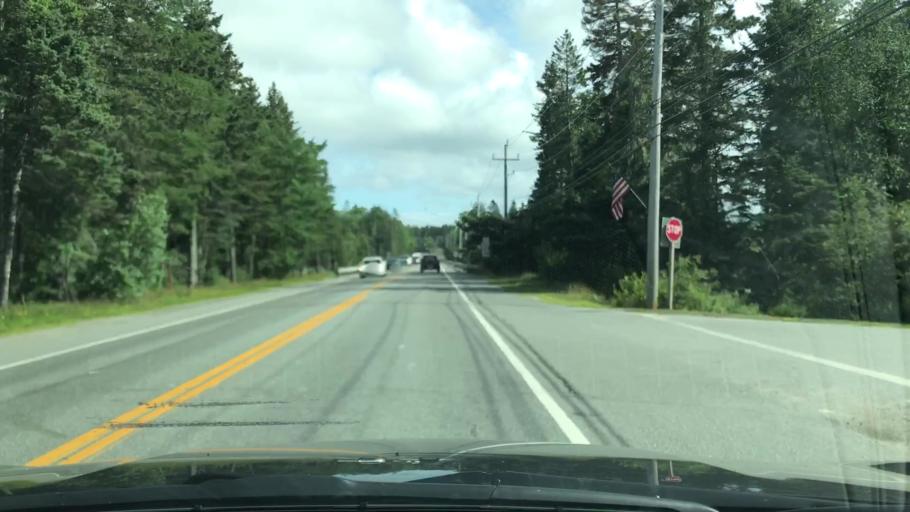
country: US
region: Maine
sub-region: Hancock County
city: Trenton
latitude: 44.4269
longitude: -68.3661
